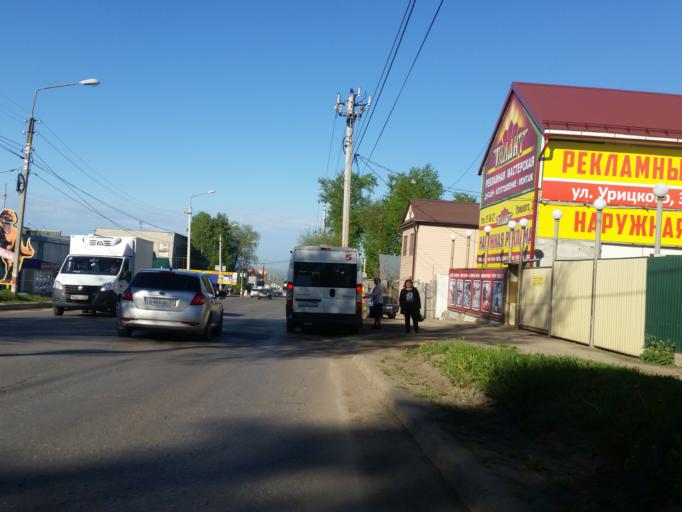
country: RU
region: Ulyanovsk
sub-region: Ulyanovskiy Rayon
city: Ulyanovsk
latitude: 54.3349
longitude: 48.3751
